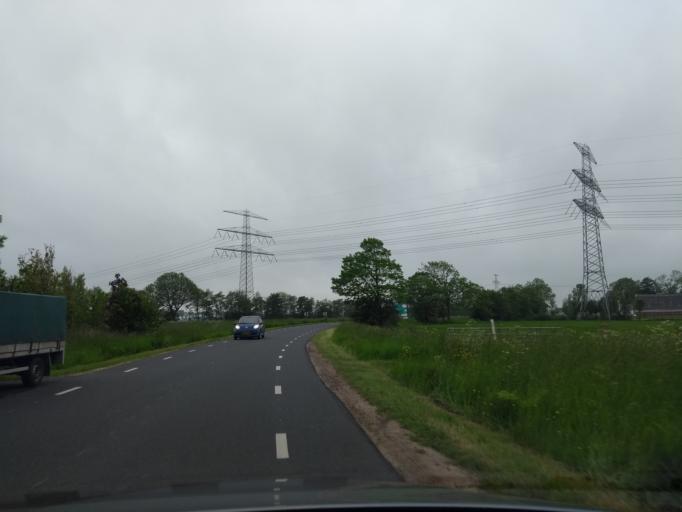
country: NL
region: Groningen
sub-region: Gemeente Zuidhorn
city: Aduard
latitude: 53.2610
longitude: 6.4794
